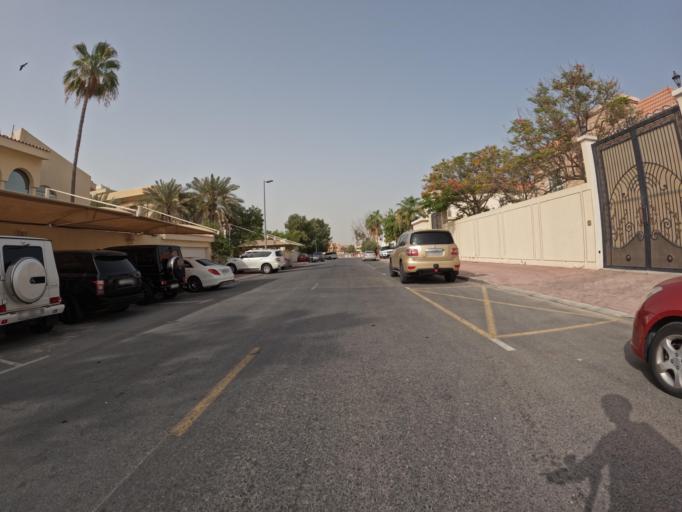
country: AE
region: Dubai
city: Dubai
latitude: 25.1967
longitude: 55.2387
